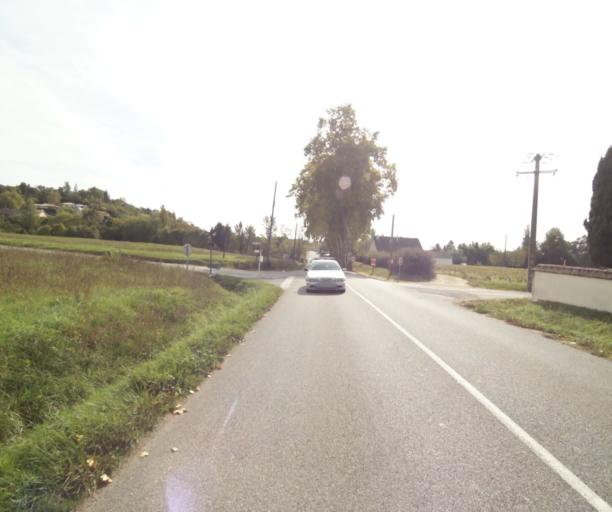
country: FR
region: Midi-Pyrenees
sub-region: Departement du Tarn-et-Garonne
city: Corbarieu
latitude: 43.9473
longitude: 1.3657
